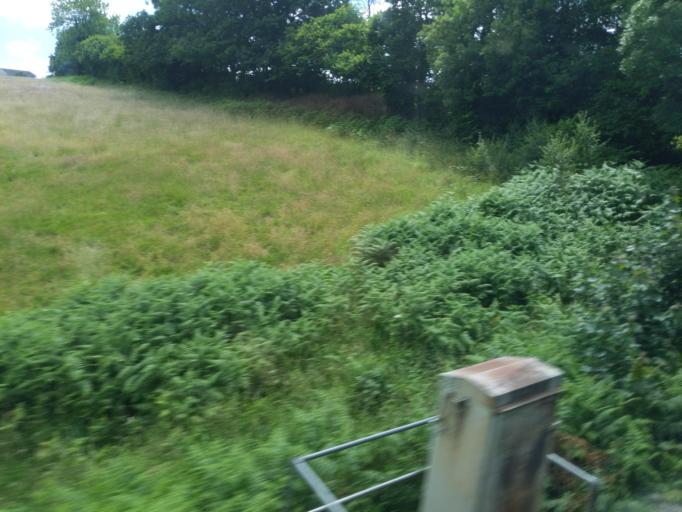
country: GB
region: England
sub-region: Cornwall
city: Par
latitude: 50.3616
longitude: -4.6969
